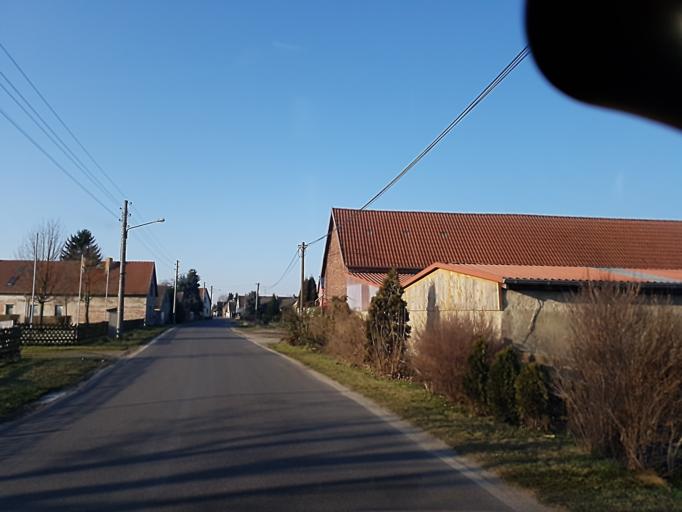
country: DE
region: Brandenburg
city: Schonborn
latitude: 51.5681
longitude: 13.5156
